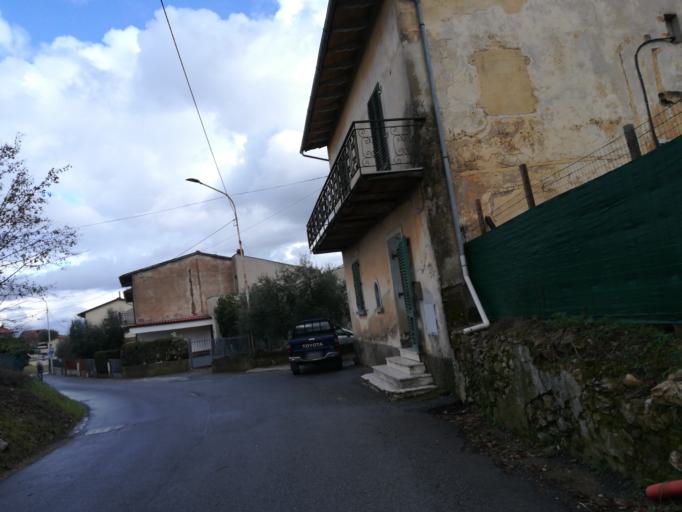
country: IT
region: Tuscany
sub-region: Provincia di Prato
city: Poggio A Caiano
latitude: 43.8083
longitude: 11.0520
